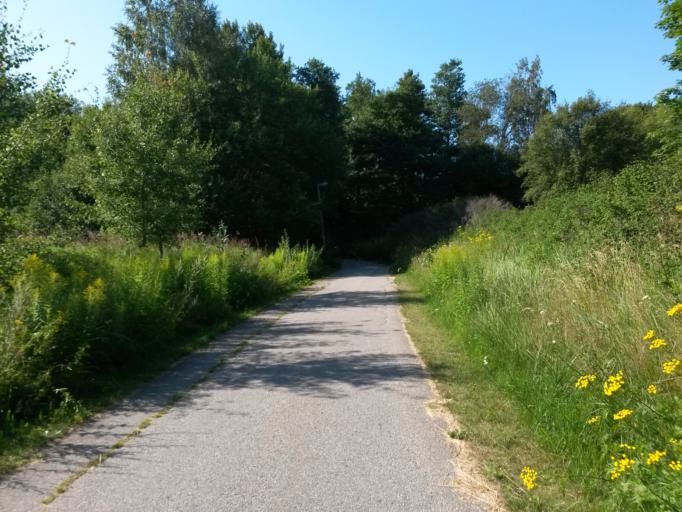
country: SE
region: Vaestra Goetaland
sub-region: Lidkopings Kommun
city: Vinninga
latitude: 58.4918
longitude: 13.2371
